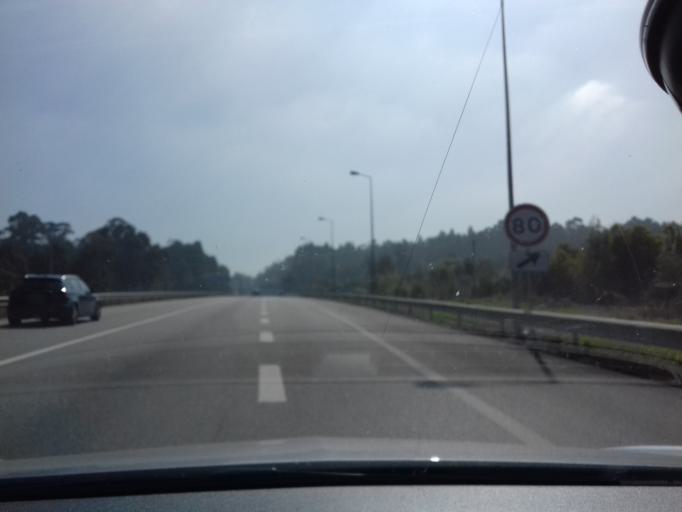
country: PT
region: Aveiro
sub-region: Santa Maria da Feira
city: Nogueira da Regedoura
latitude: 41.0084
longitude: -8.6067
